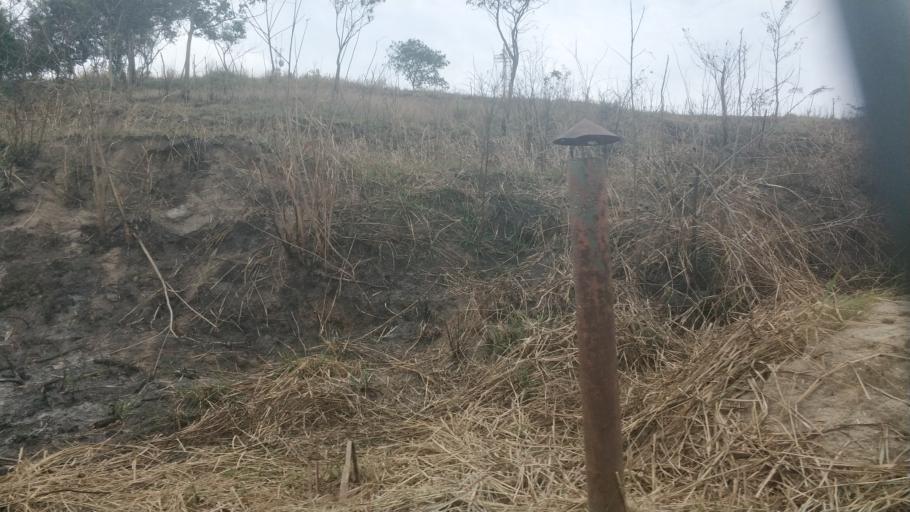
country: BR
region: Rio de Janeiro
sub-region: Seropedica
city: Seropedica
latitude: -22.8142
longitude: -43.6327
